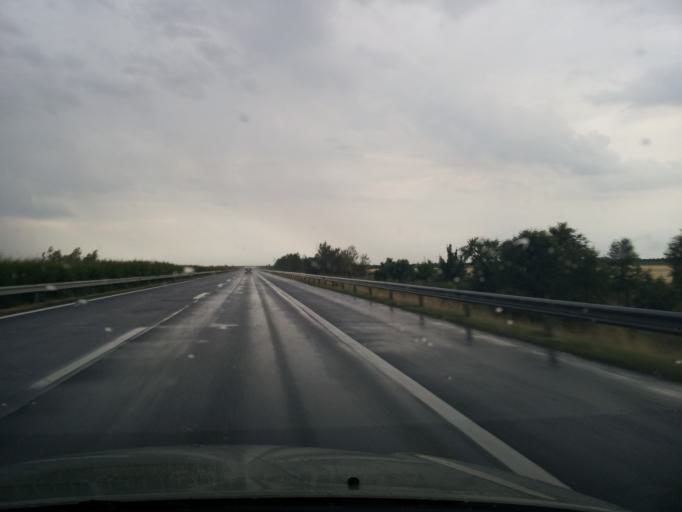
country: HU
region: Borsod-Abauj-Zemplen
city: Onod
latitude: 48.0104
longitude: 20.8791
